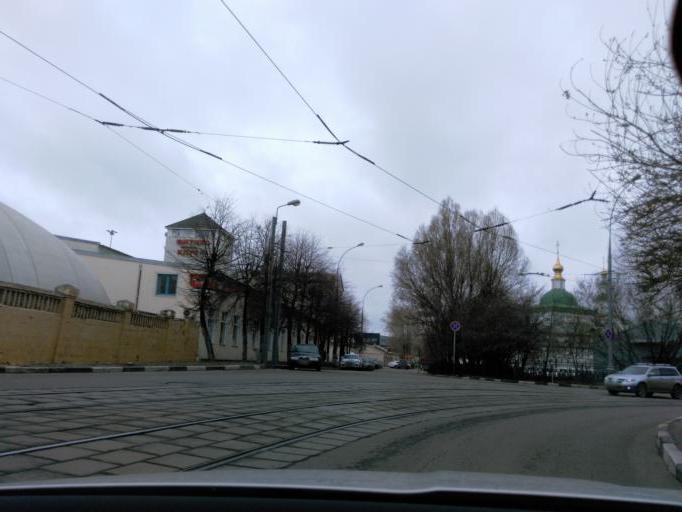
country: RU
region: Moscow
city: Zamoskvorech'ye
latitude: 55.7119
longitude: 37.6329
